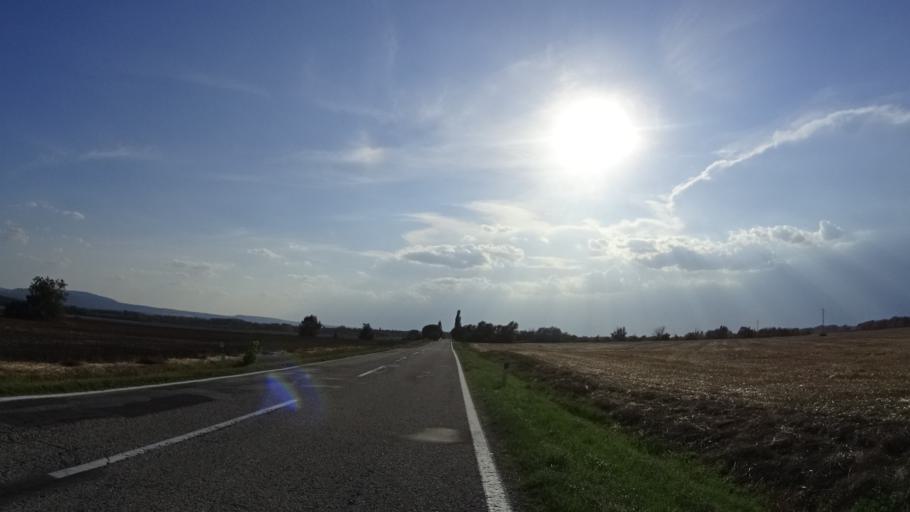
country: HU
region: Komarom-Esztergom
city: Nyergesujfalu
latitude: 47.7858
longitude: 18.5892
